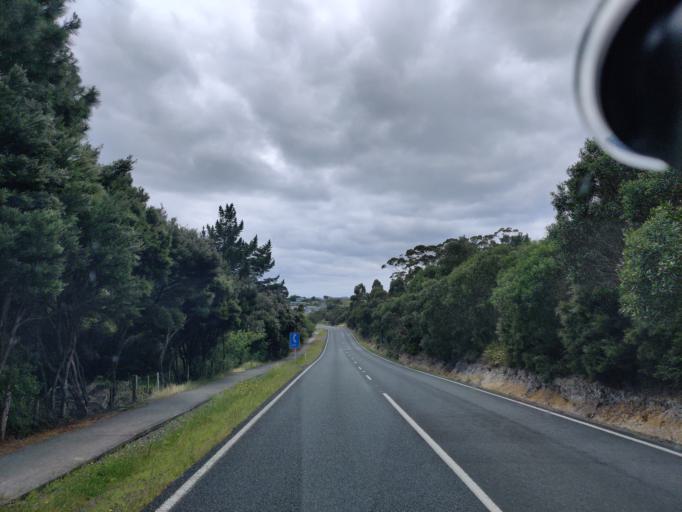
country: NZ
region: Northland
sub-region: Far North District
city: Kaitaia
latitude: -34.6551
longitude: 172.9690
